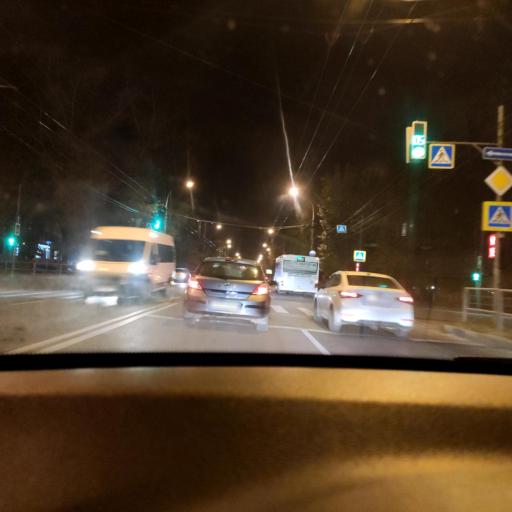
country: RU
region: Samara
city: Samara
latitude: 53.2218
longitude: 50.2598
